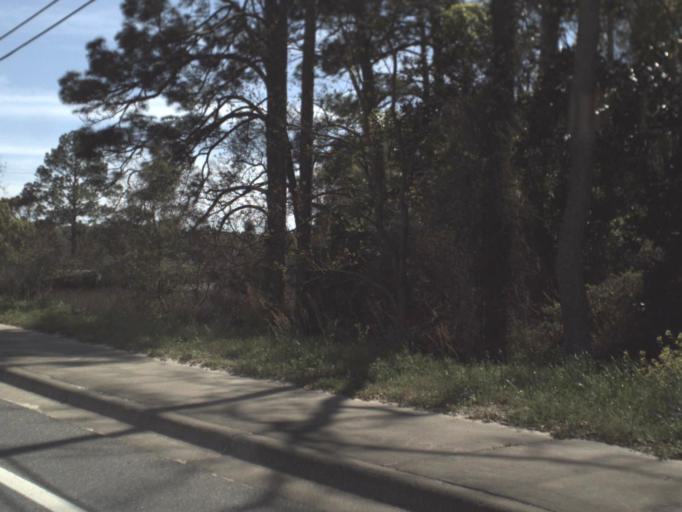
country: US
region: Florida
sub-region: Bay County
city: Lynn Haven
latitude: 30.2887
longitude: -85.6405
